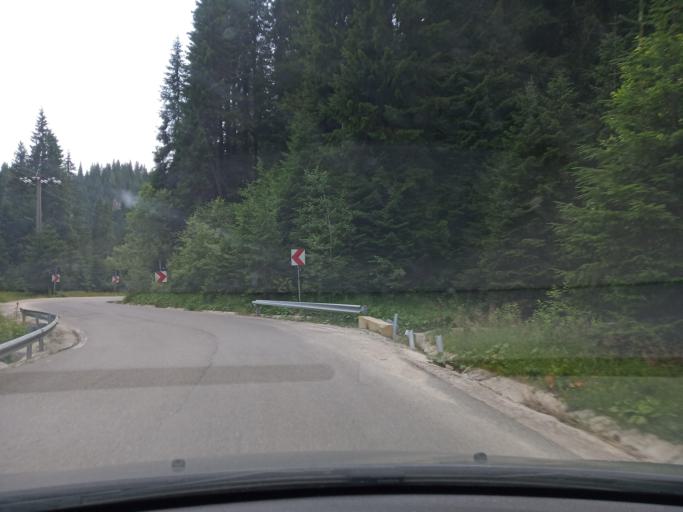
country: RO
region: Dambovita
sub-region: Comuna Moroeni
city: Glod
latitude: 45.3379
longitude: 25.4252
